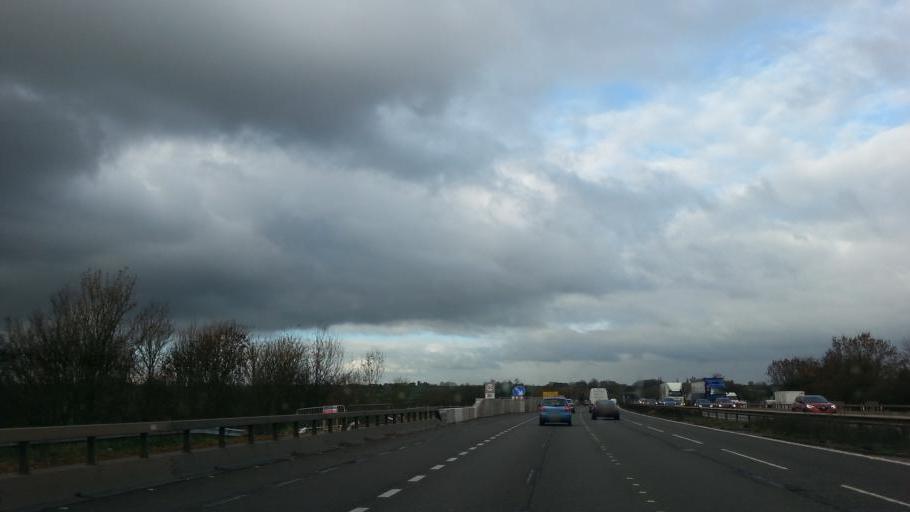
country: GB
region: England
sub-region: Staffordshire
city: Stafford
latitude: 52.7661
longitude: -2.1110
